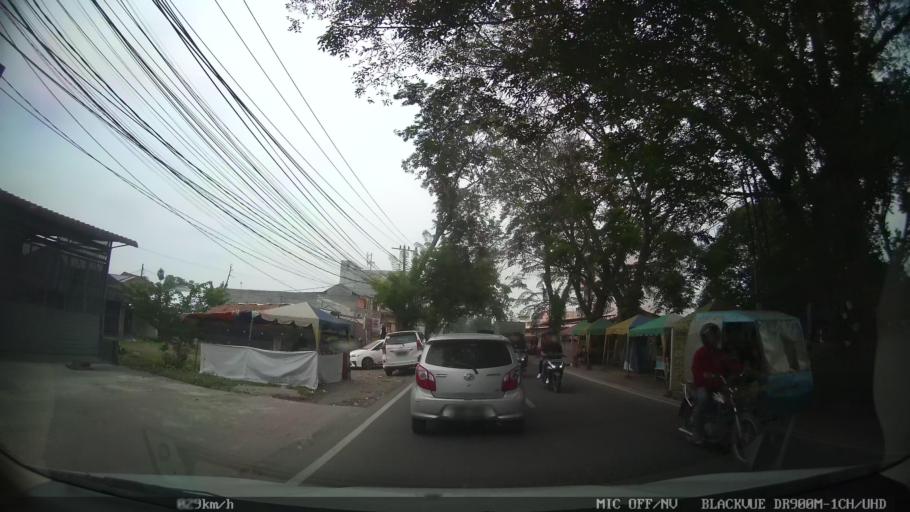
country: ID
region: North Sumatra
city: Medan
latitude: 3.5685
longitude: 98.7043
